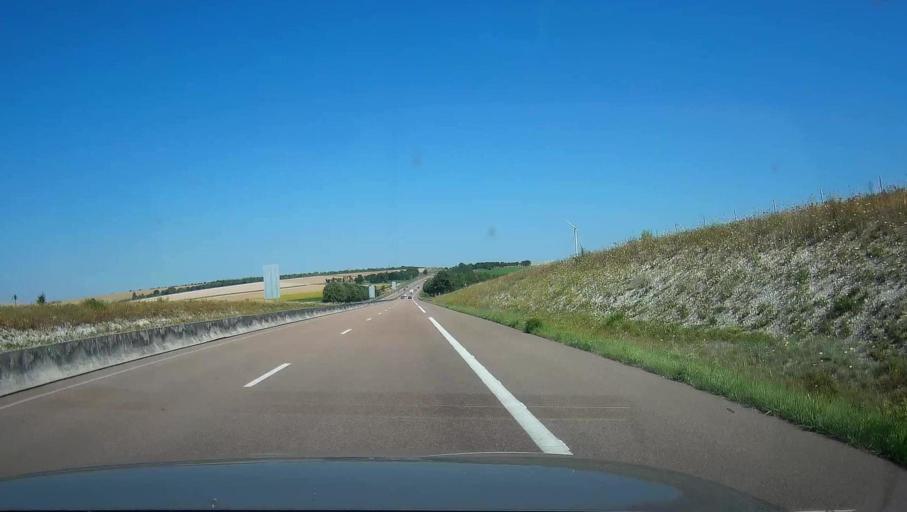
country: FR
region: Champagne-Ardenne
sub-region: Departement de l'Aube
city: Arcis-sur-Aube
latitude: 48.4458
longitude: 4.1569
